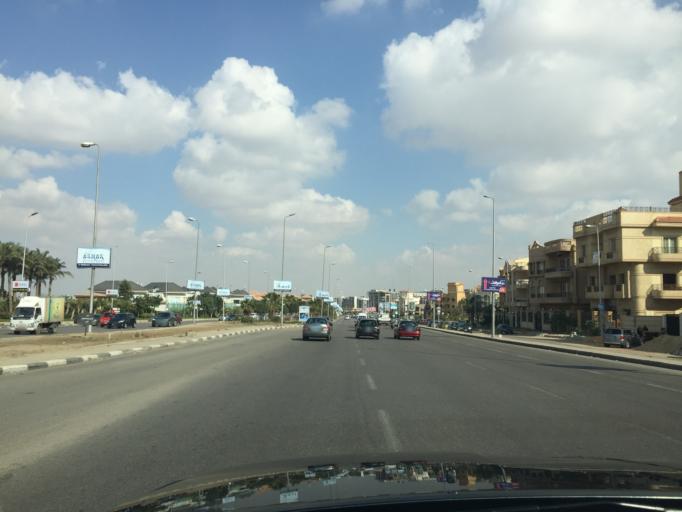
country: EG
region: Muhafazat al Qahirah
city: Cairo
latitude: 30.0213
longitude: 31.4517
